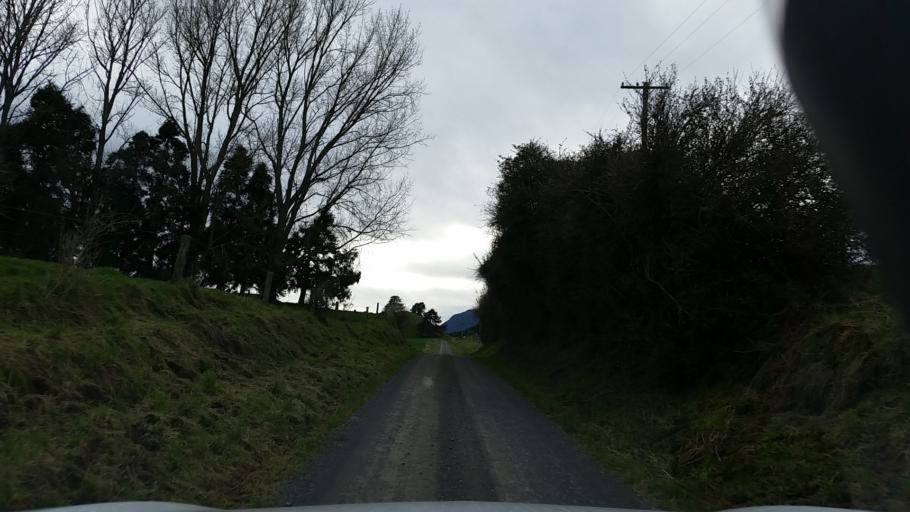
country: NZ
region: Bay of Plenty
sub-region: Rotorua District
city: Rotorua
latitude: -38.3055
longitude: 176.4167
